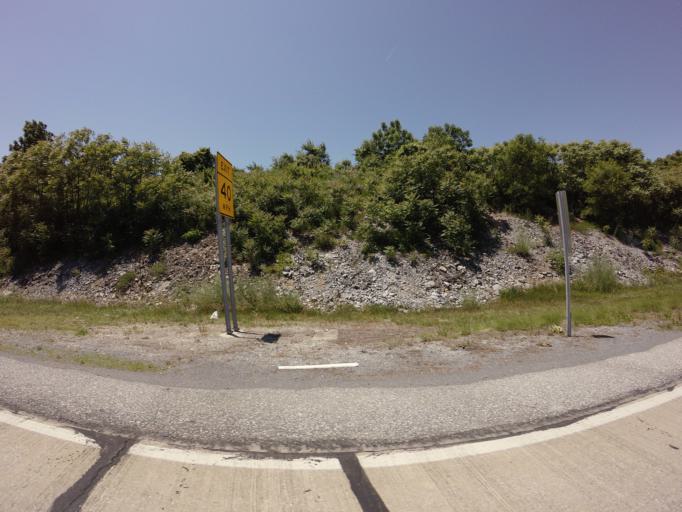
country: US
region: West Virginia
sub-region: Jefferson County
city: Ranson
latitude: 39.2999
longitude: -77.8406
